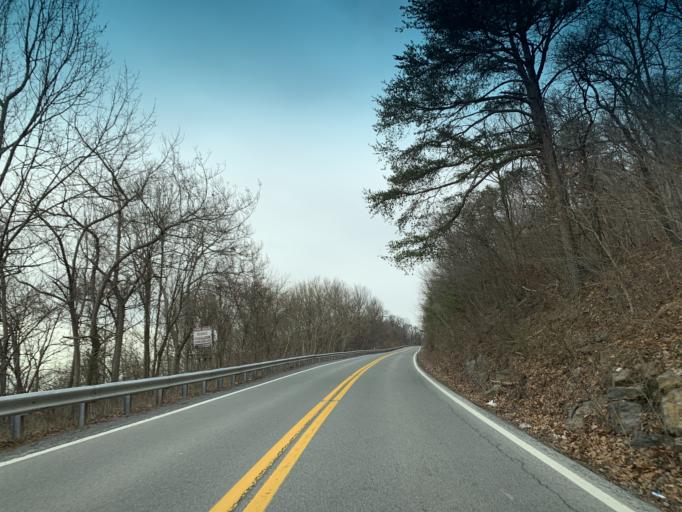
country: US
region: West Virginia
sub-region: Jefferson County
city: Shannondale
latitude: 39.2577
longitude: -77.7746
